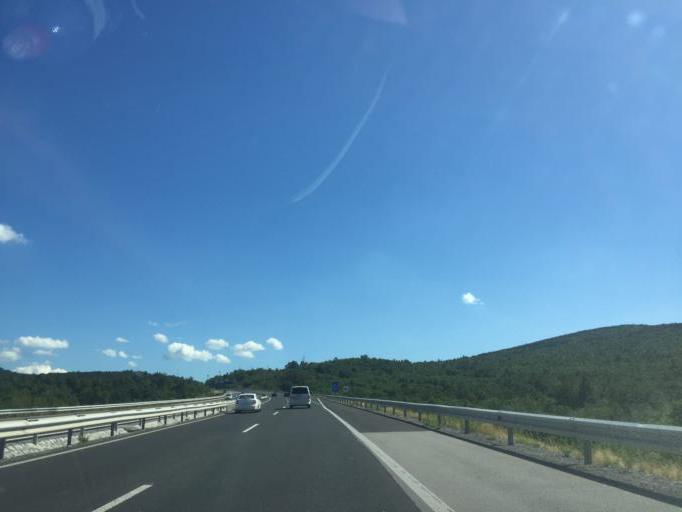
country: SI
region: Divaca
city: Divaca
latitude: 45.6498
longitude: 13.9600
